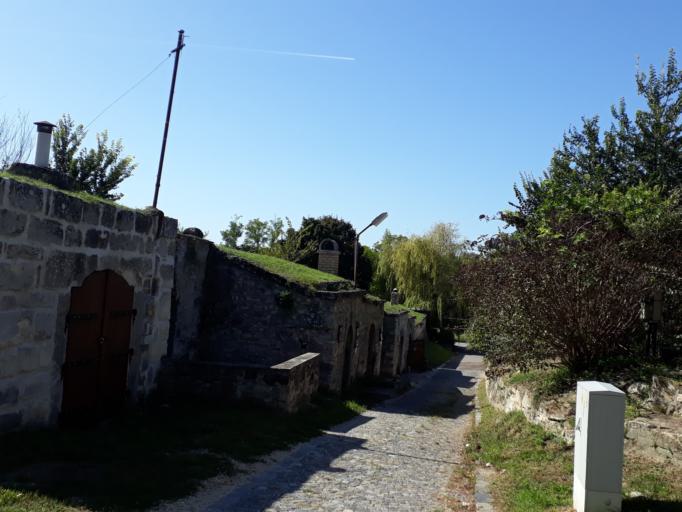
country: HU
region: Fejer
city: Etyek
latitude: 47.4445
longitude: 18.7591
